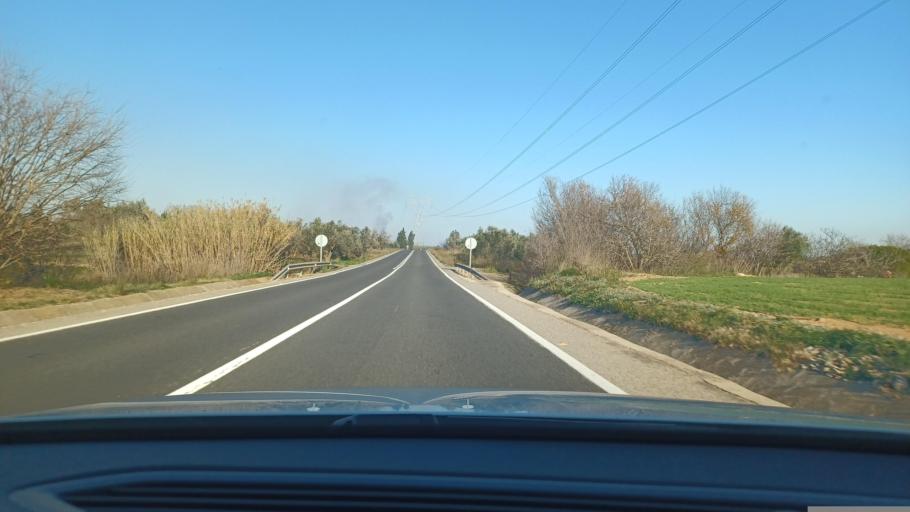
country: ES
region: Catalonia
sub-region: Provincia de Tarragona
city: Santa Barbara
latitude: 40.6746
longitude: 0.4477
